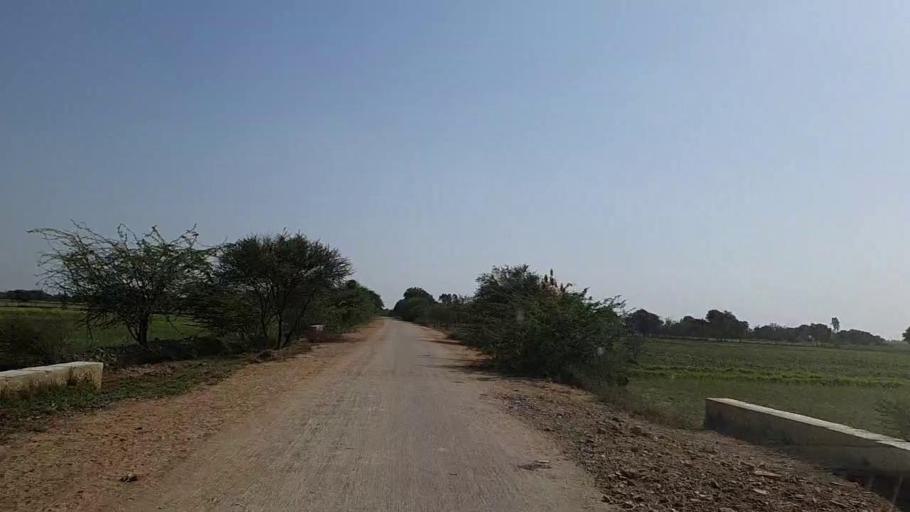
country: PK
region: Sindh
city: Daro Mehar
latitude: 24.7574
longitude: 68.1821
